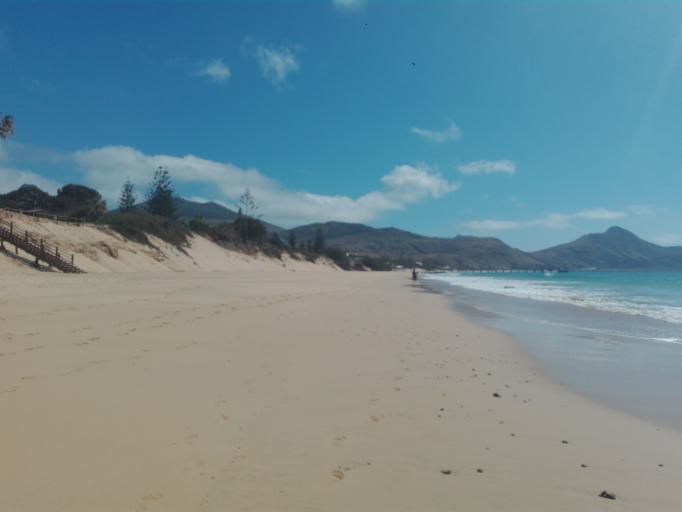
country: PT
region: Madeira
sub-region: Porto Santo
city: Vila de Porto Santo
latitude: 33.0533
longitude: -16.3419
